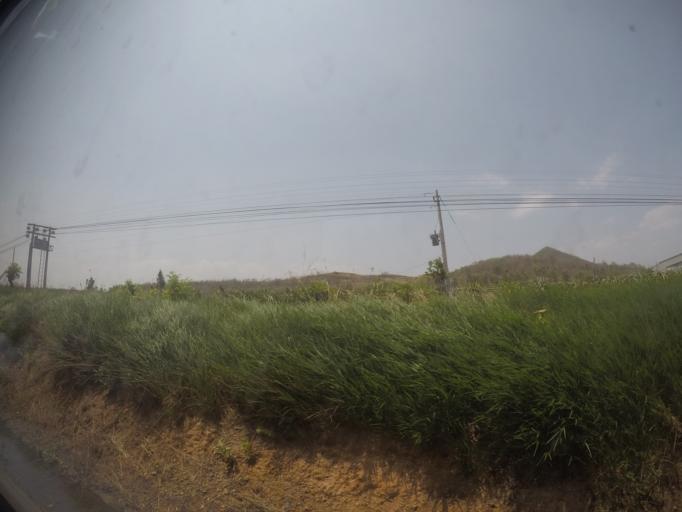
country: VN
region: Binh Thuan
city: Thuan Nam
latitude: 10.9378
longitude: 107.9678
